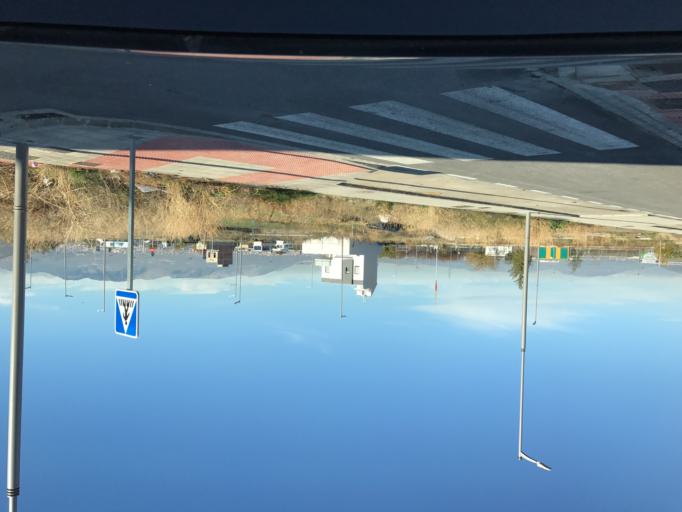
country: ES
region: Andalusia
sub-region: Provincia de Granada
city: Churriana de la Vega
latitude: 37.1485
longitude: -3.6535
